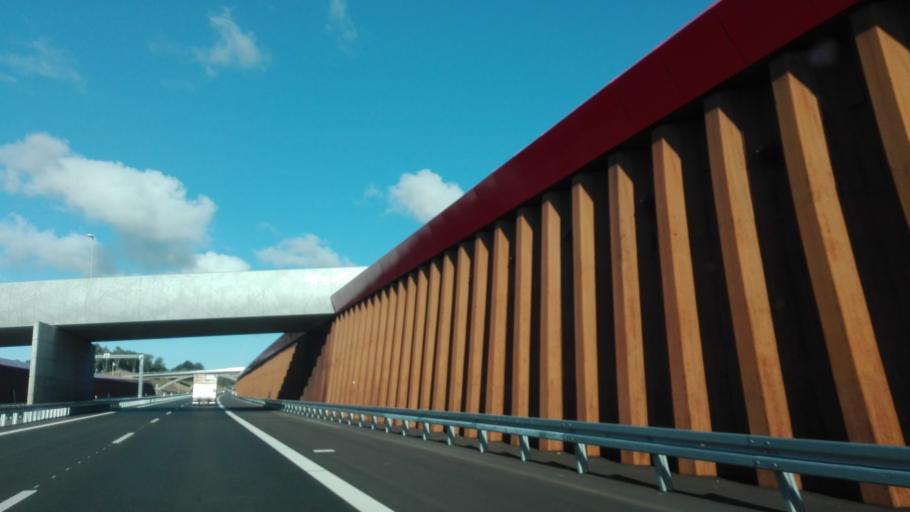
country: DK
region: Central Jutland
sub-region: Silkeborg Kommune
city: Silkeborg
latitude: 56.1885
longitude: 9.5713
